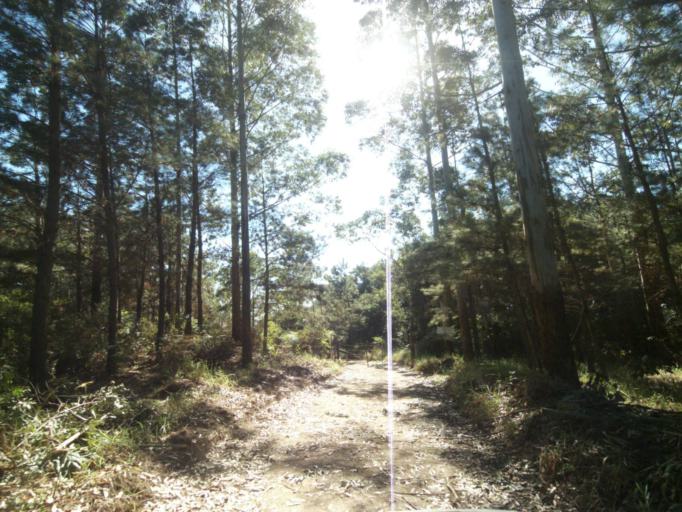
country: BR
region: Parana
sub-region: Tibagi
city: Tibagi
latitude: -24.5538
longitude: -50.4755
